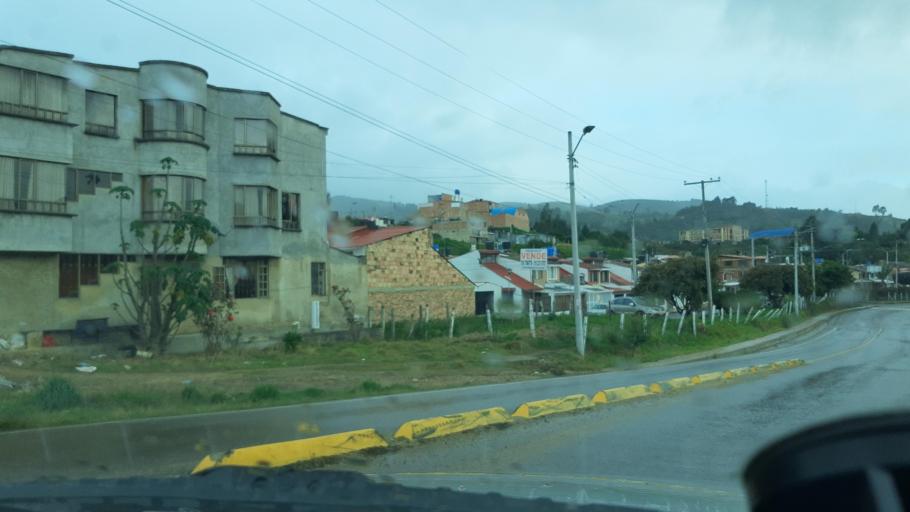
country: CO
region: Cundinamarca
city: Villapinzon
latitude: 5.2228
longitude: -73.5919
